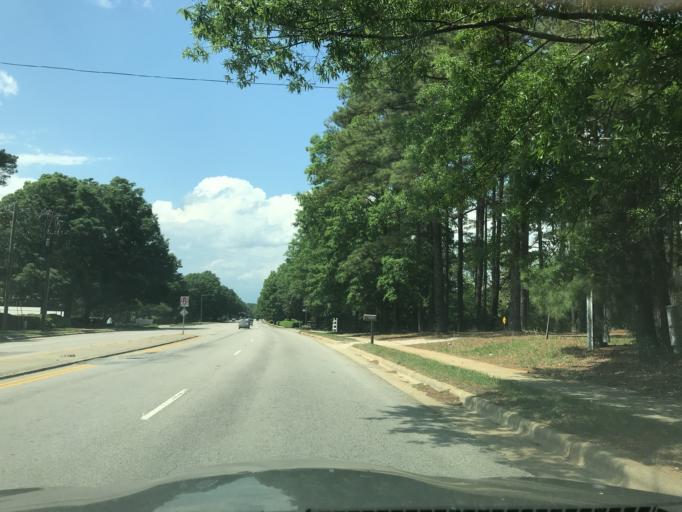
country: US
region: North Carolina
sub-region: Wake County
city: West Raleigh
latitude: 35.8682
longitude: -78.6387
